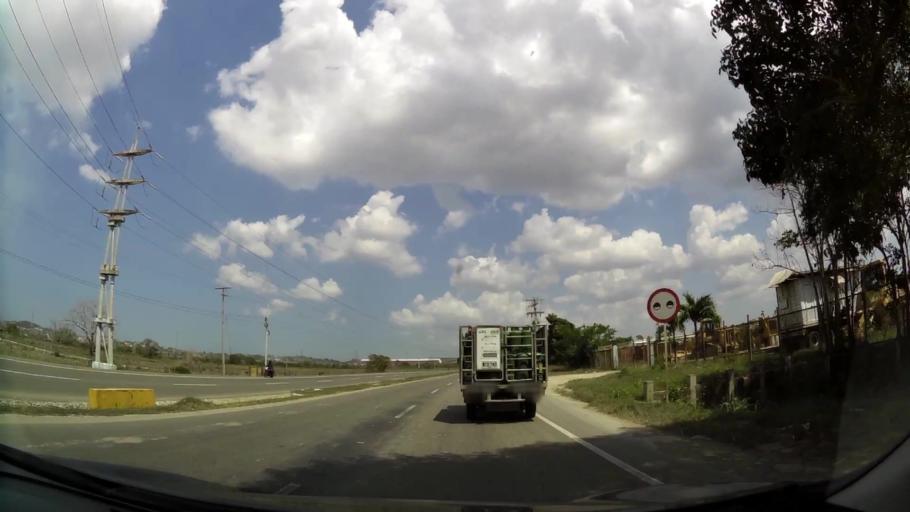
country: CO
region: Bolivar
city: Cartagena
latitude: 10.3511
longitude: -75.4811
